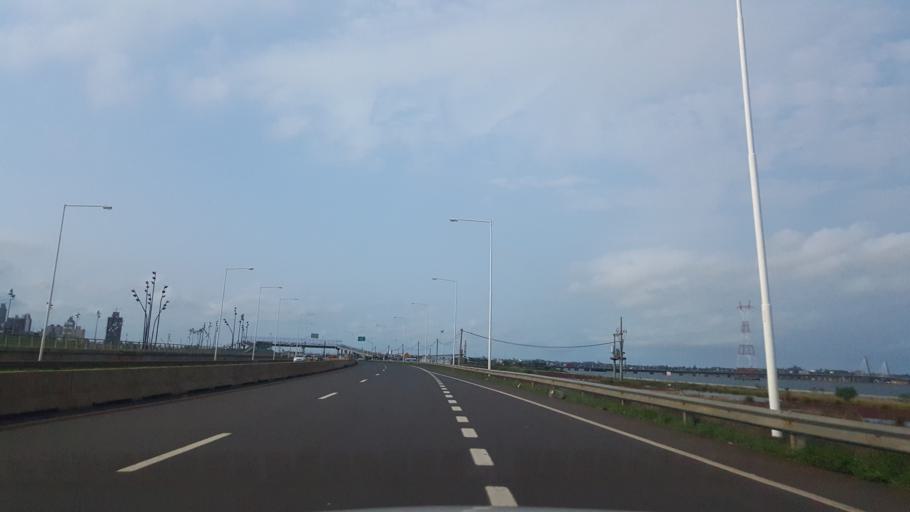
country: AR
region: Misiones
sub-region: Departamento de Capital
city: Posadas
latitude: -27.3834
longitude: -55.8854
